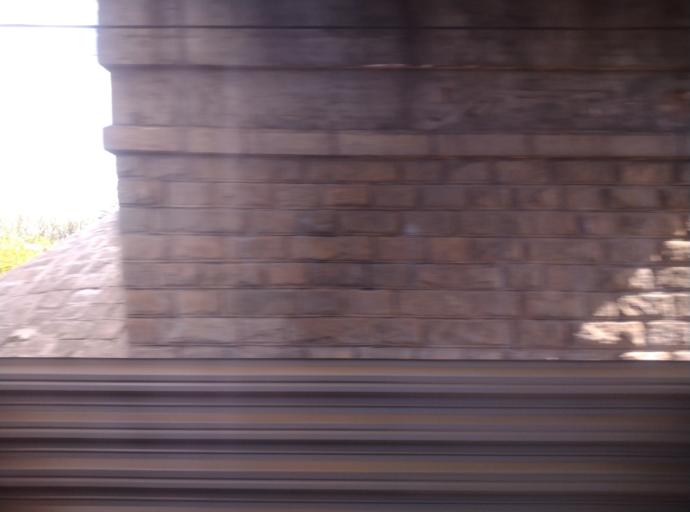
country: RU
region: St.-Petersburg
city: Kupchino
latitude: 59.8811
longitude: 30.4054
